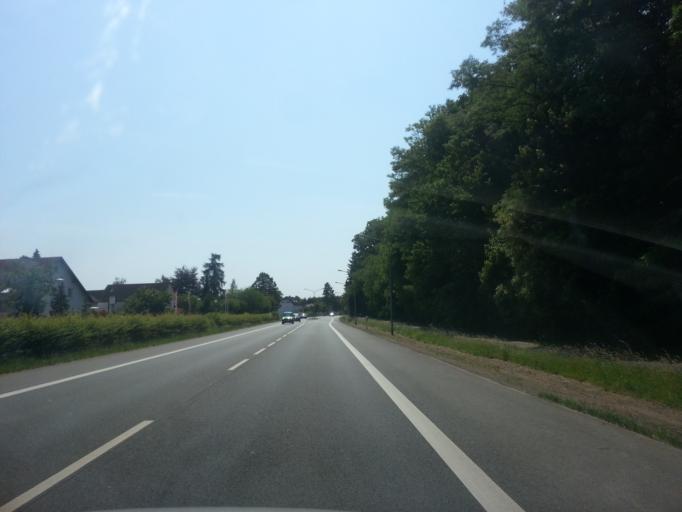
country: DE
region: Hesse
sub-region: Regierungsbezirk Darmstadt
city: Dietzenbach
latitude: 50.0005
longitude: 8.8162
